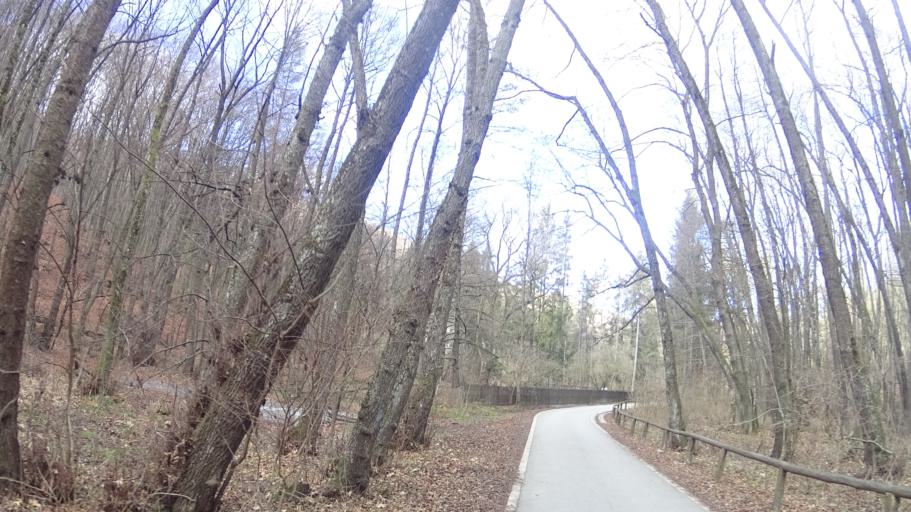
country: HU
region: Heves
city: Szilvasvarad
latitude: 48.0798
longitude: 20.4063
